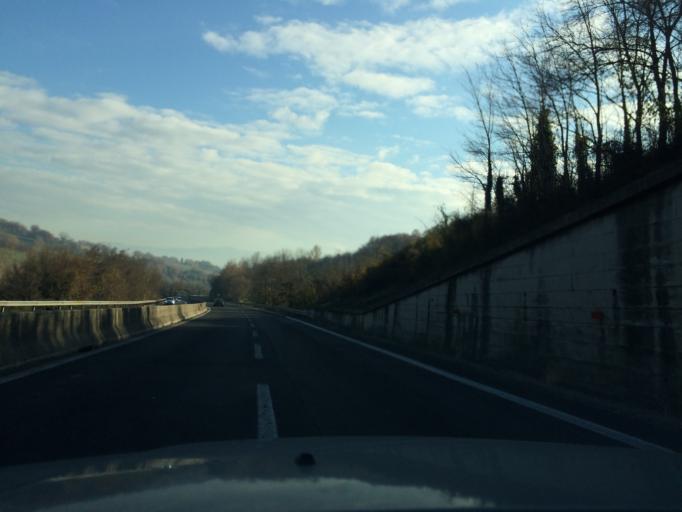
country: IT
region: Umbria
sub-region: Provincia di Terni
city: San Gemini
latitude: 42.6061
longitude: 12.5580
